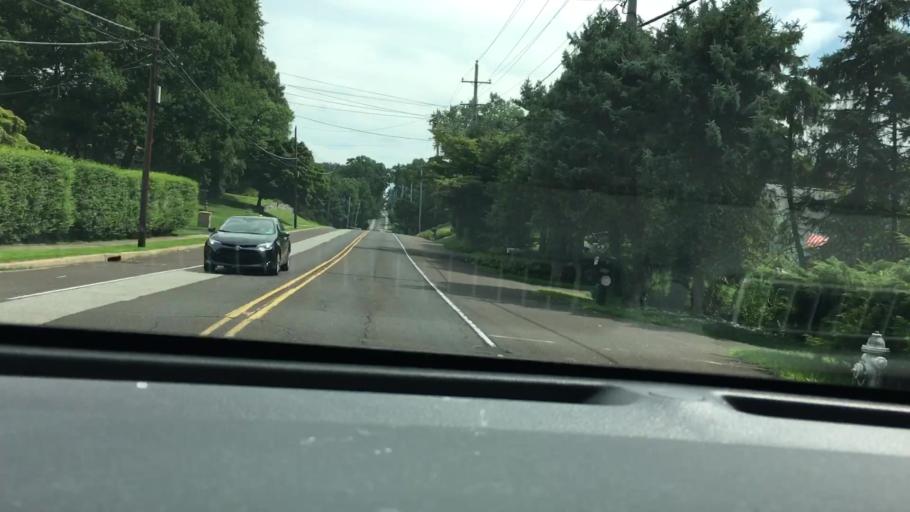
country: US
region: Pennsylvania
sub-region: Montgomery County
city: Bryn Athyn
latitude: 40.1381
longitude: -75.0398
